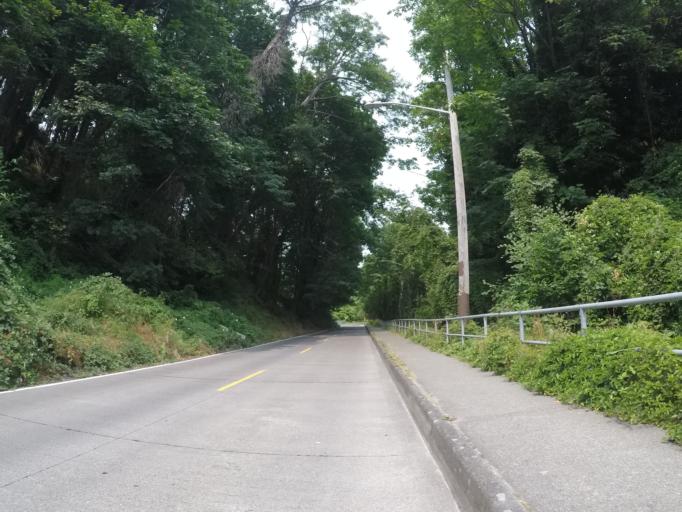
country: US
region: Washington
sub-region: King County
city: Seattle
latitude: 47.5923
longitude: -122.3838
